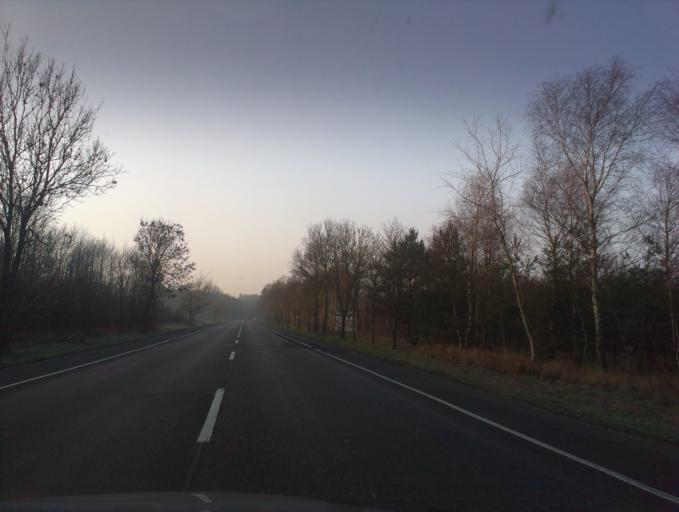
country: PL
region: Greater Poland Voivodeship
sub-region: Powiat obornicki
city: Rogozno
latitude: 52.7287
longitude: 16.9383
